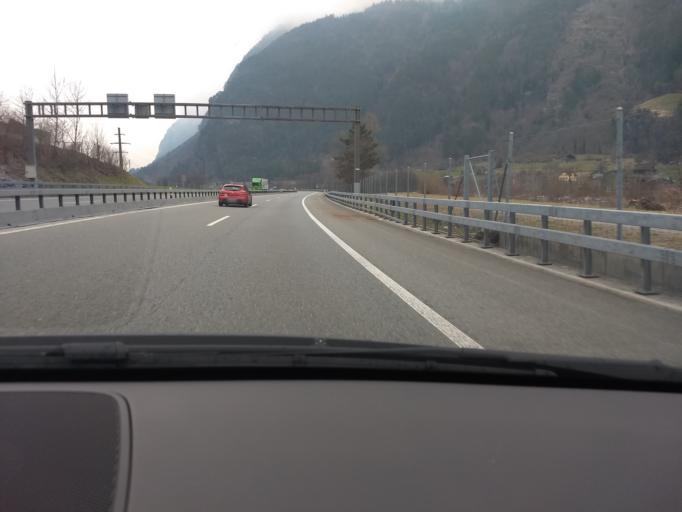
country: CH
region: Uri
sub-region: Uri
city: Erstfeld
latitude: 46.8044
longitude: 8.6606
